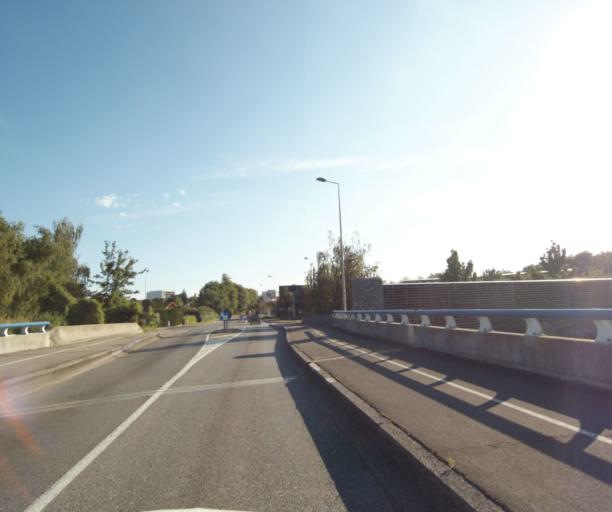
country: FR
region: Rhone-Alpes
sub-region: Departement de la Haute-Savoie
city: Thonon-les-Bains
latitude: 46.3546
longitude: 6.4697
